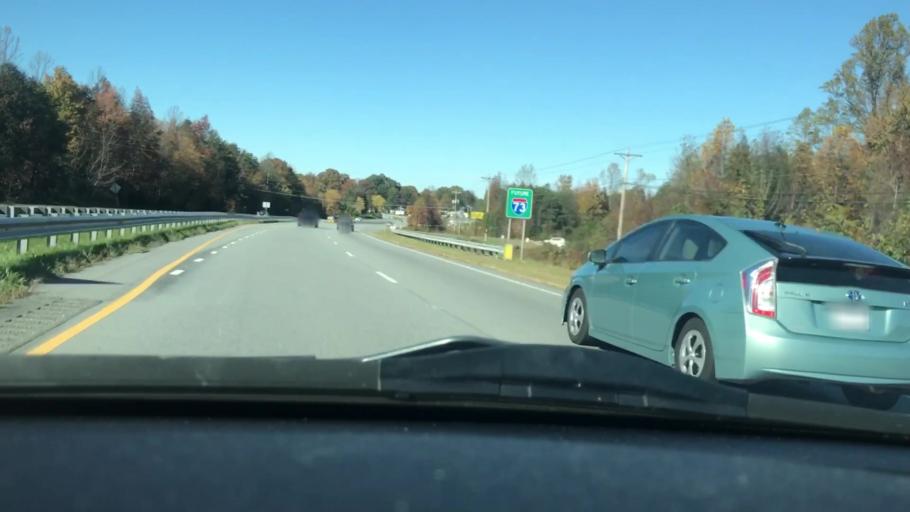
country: US
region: North Carolina
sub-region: Rockingham County
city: Madison
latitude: 36.3266
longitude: -79.9465
